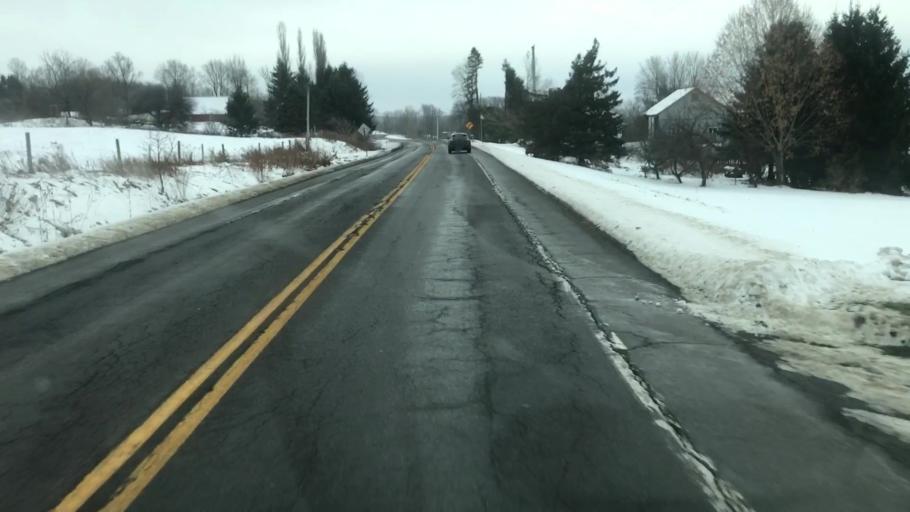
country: US
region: New York
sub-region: Cayuga County
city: Moravia
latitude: 42.7384
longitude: -76.3159
